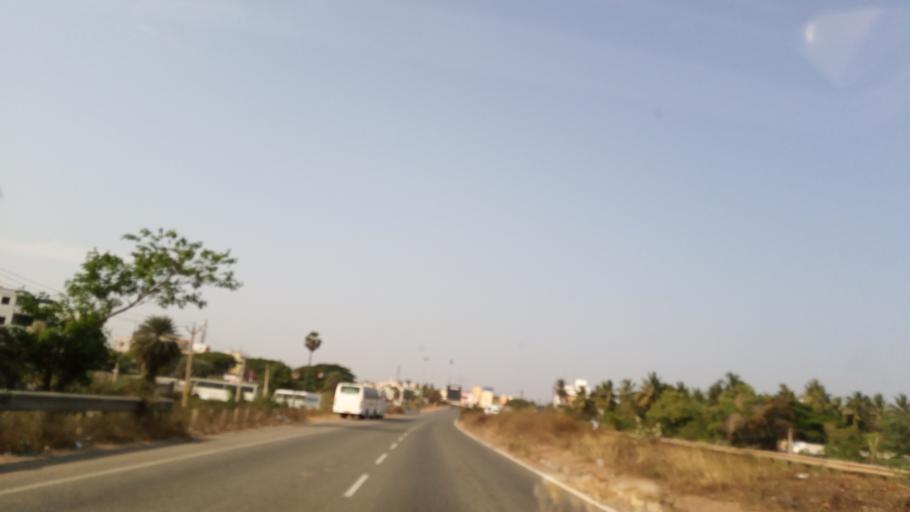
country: IN
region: Tamil Nadu
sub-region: Kancheepuram
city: Sriperumbudur
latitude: 12.9726
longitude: 79.9558
